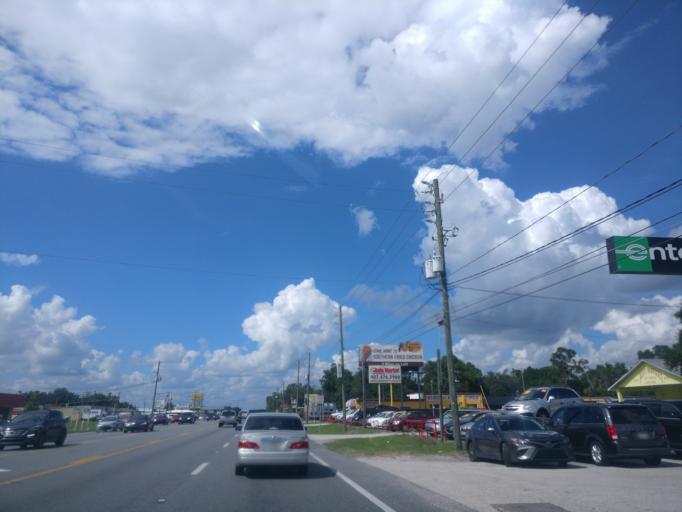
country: US
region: Florida
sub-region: Osceola County
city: Kissimmee
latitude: 28.3270
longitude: -81.4037
